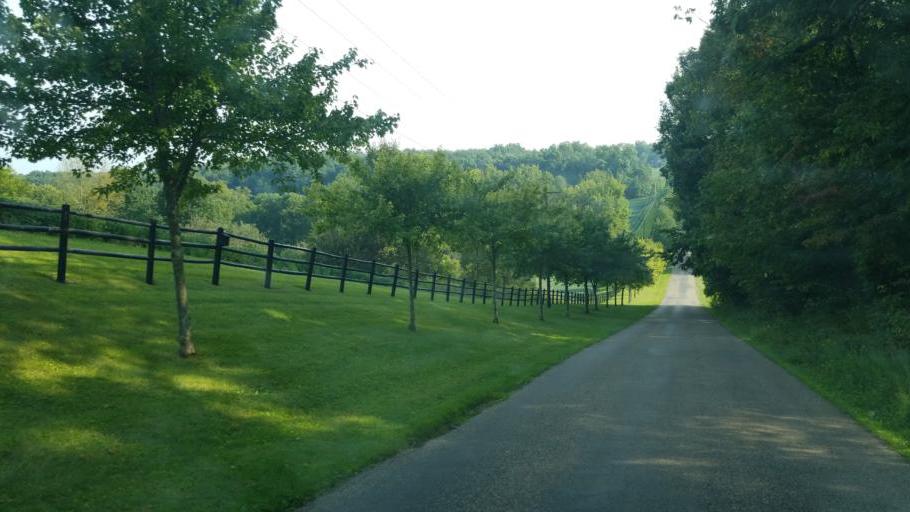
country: US
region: Ohio
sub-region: Knox County
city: Gambier
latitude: 40.3622
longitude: -82.4095
